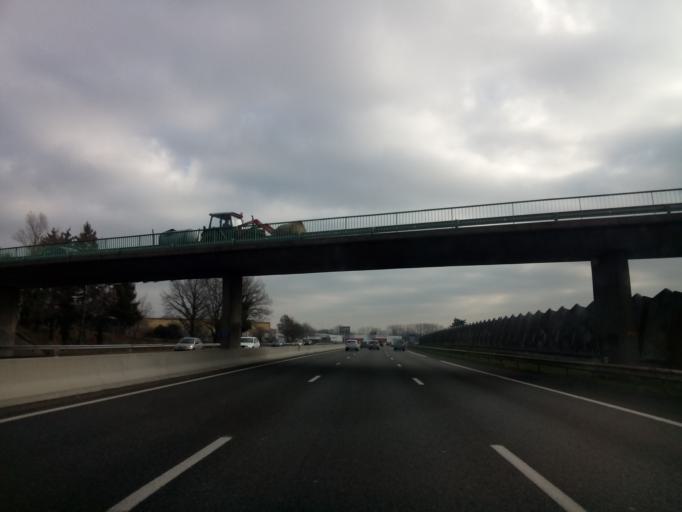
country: FR
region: Rhone-Alpes
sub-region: Departement de l'Isere
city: La Verpilliere
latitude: 45.6456
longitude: 5.1342
